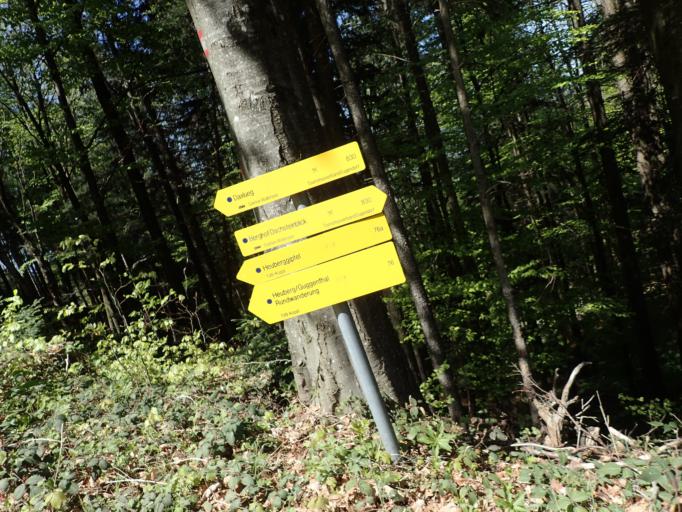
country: AT
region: Salzburg
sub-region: Politischer Bezirk Salzburg-Umgebung
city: Hallwang
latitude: 47.8328
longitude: 13.1121
